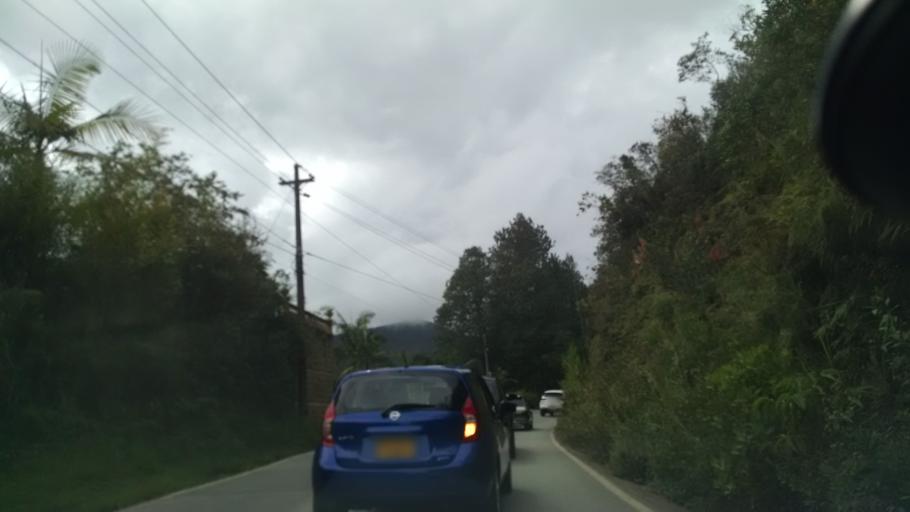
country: CO
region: Antioquia
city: Guatape
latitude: 6.2081
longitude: -75.2205
